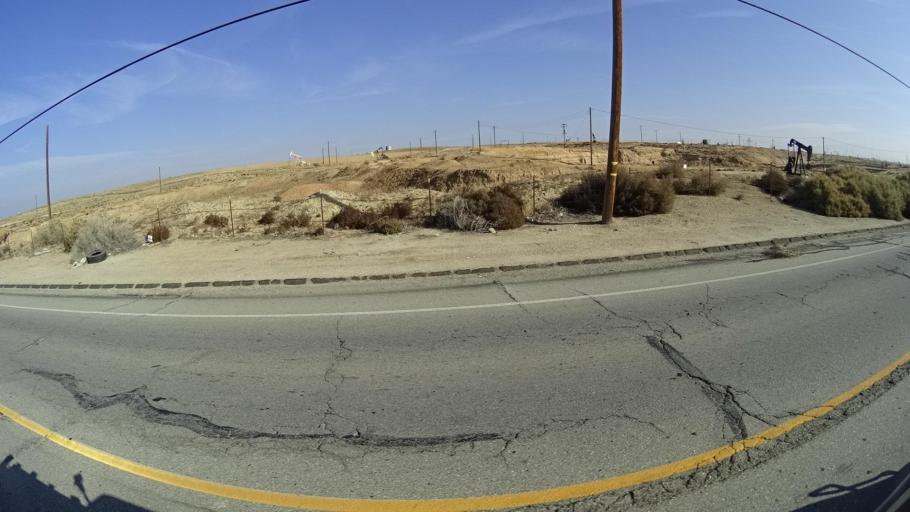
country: US
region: California
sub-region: Kern County
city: Oildale
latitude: 35.4683
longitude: -119.0635
